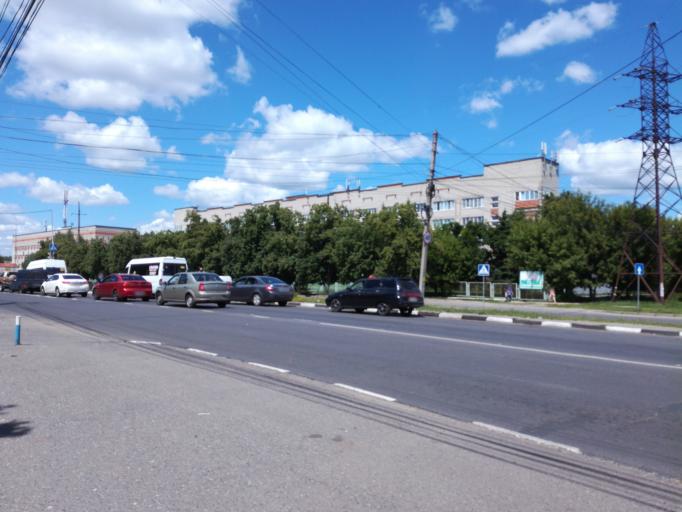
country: RU
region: Kursk
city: Kursk
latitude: 51.7455
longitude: 36.2587
